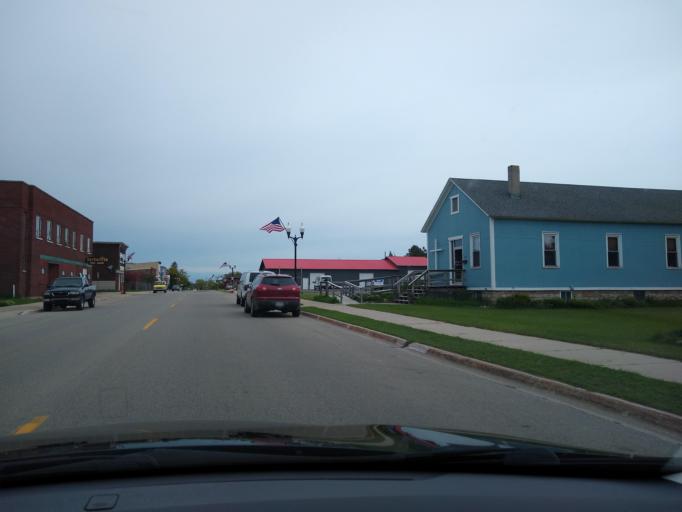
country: US
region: Michigan
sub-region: Delta County
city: Escanaba
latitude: 45.7640
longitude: -87.0691
